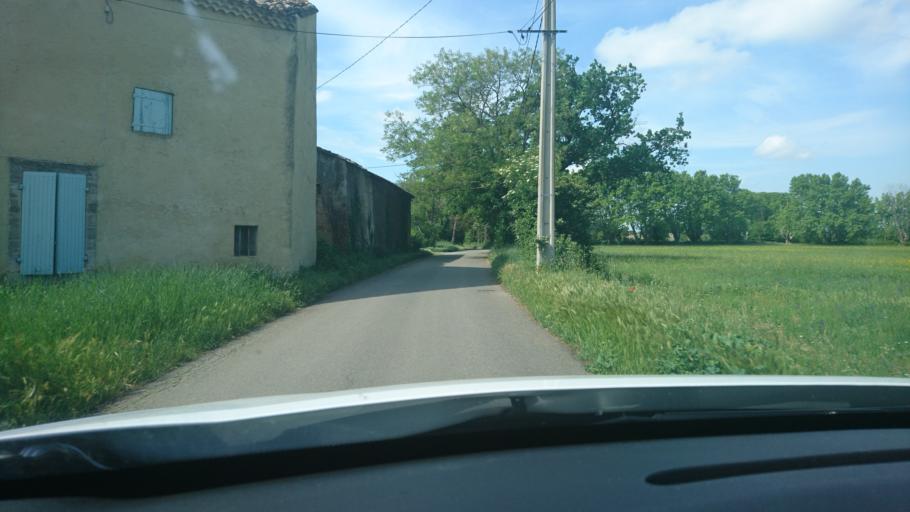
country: FR
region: Provence-Alpes-Cote d'Azur
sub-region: Departement du Vaucluse
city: Morieres-les-Avignon
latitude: 43.9354
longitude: 4.8884
